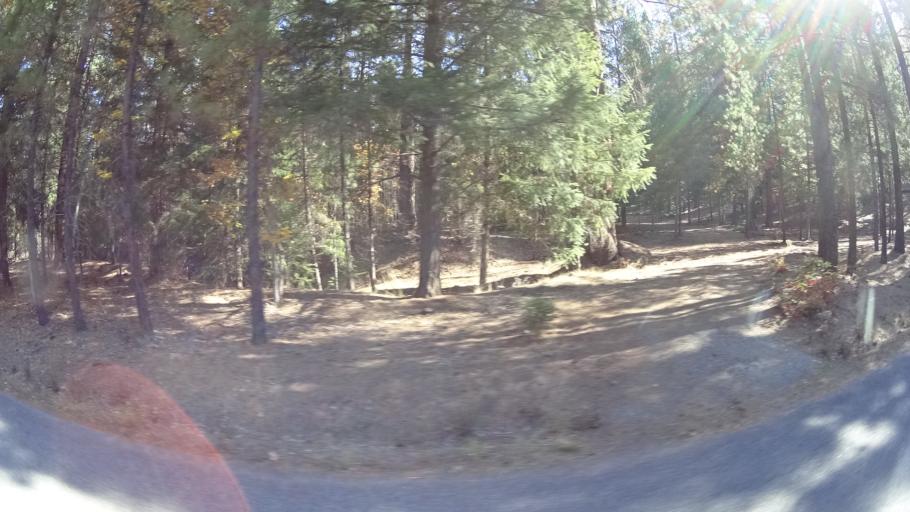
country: US
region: California
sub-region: Siskiyou County
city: Yreka
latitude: 41.6111
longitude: -122.9600
